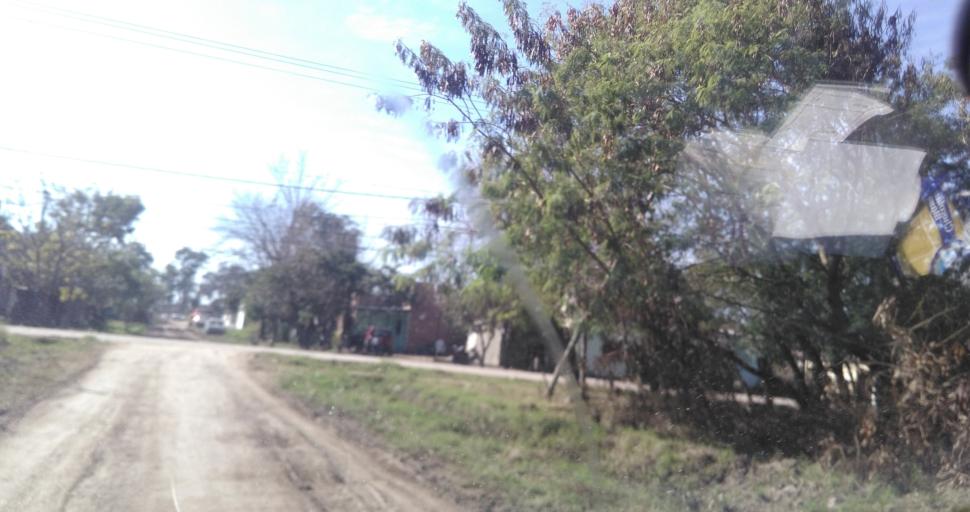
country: AR
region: Chaco
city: Fontana
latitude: -27.4446
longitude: -59.0303
